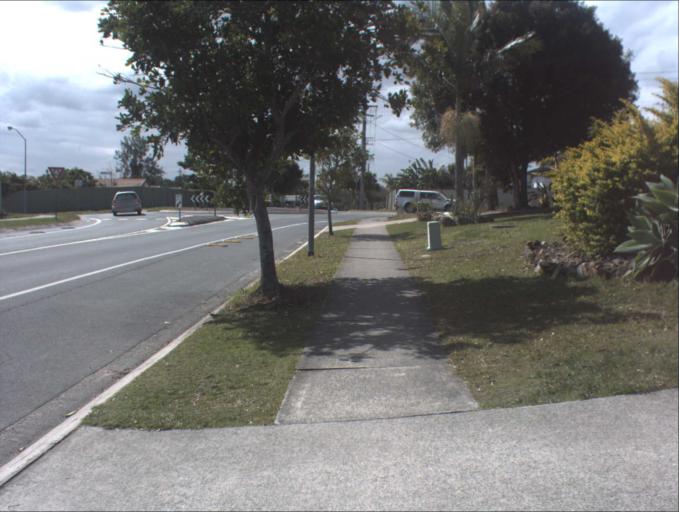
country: AU
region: Queensland
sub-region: Logan
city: Woodridge
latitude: -27.6735
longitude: 153.0815
